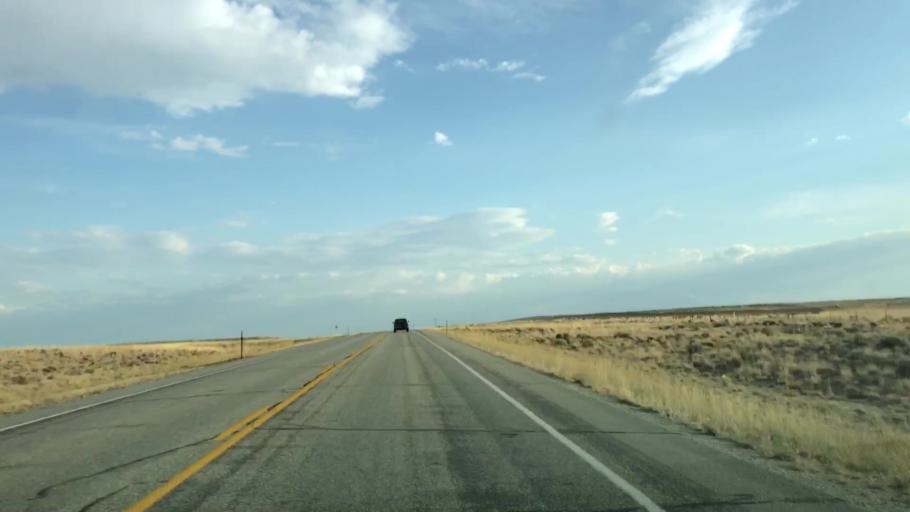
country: US
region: Wyoming
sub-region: Sublette County
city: Pinedale
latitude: 42.3437
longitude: -109.5219
